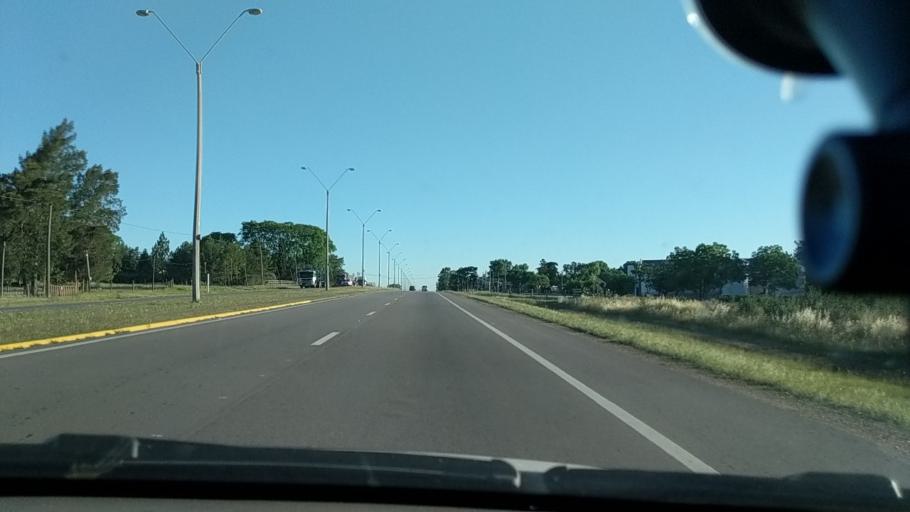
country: UY
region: Canelones
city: Joanico
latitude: -34.5842
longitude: -56.2641
